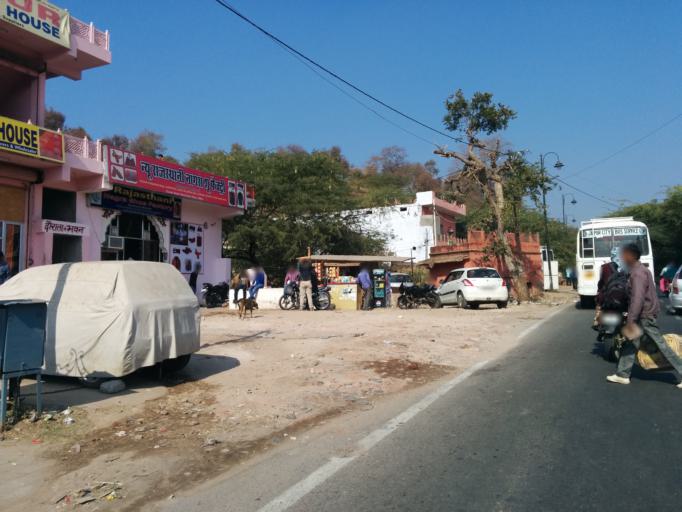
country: IN
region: Rajasthan
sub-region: Jaipur
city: Jaipur
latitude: 26.9635
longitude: 75.8463
